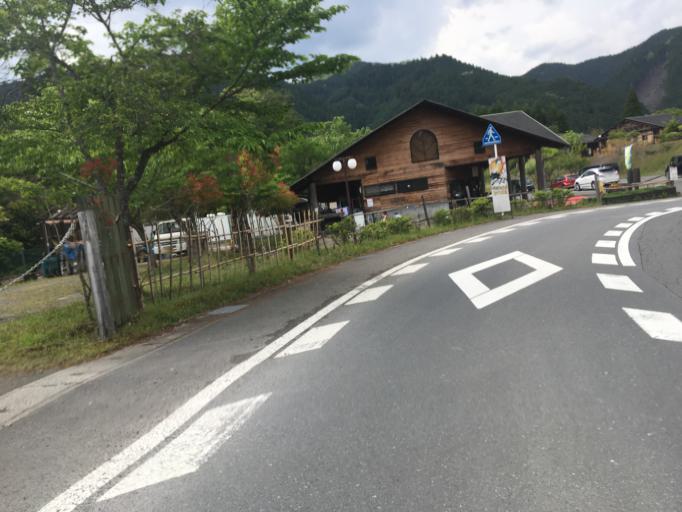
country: JP
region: Kyoto
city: Kameoka
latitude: 35.1445
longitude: 135.5742
